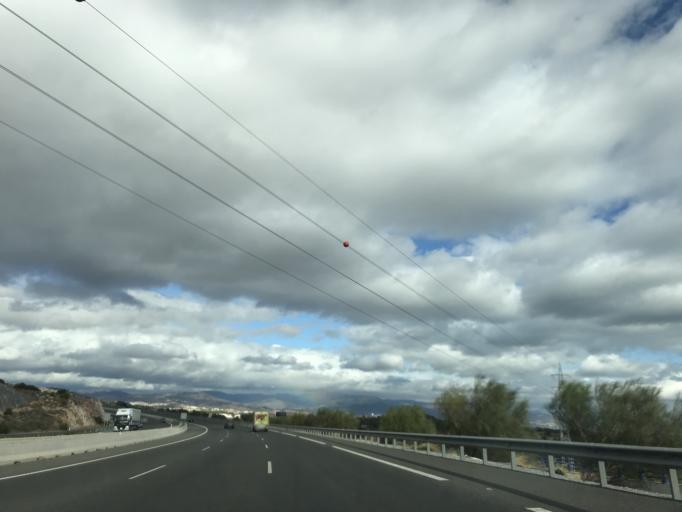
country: ES
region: Andalusia
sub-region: Provincia de Malaga
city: Torremolinos
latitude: 36.6287
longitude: -4.5153
